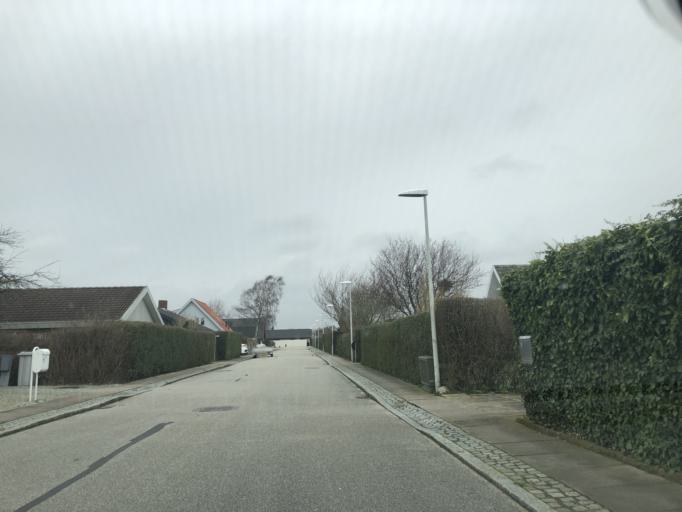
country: DK
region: Capital Region
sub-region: Tarnby Kommune
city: Tarnby
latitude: 55.6073
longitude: 12.5895
